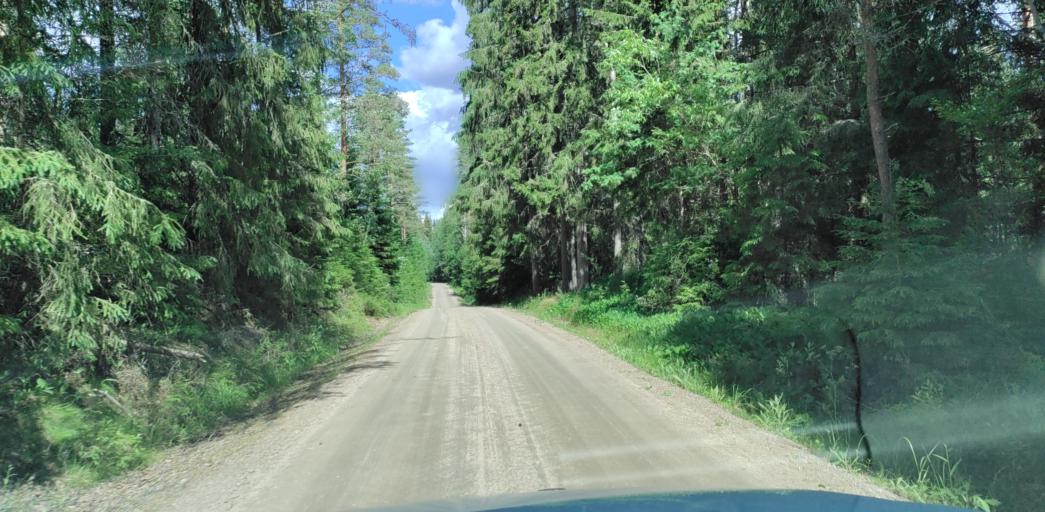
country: SE
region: Vaermland
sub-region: Sunne Kommun
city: Sunne
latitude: 60.0425
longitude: 13.2534
